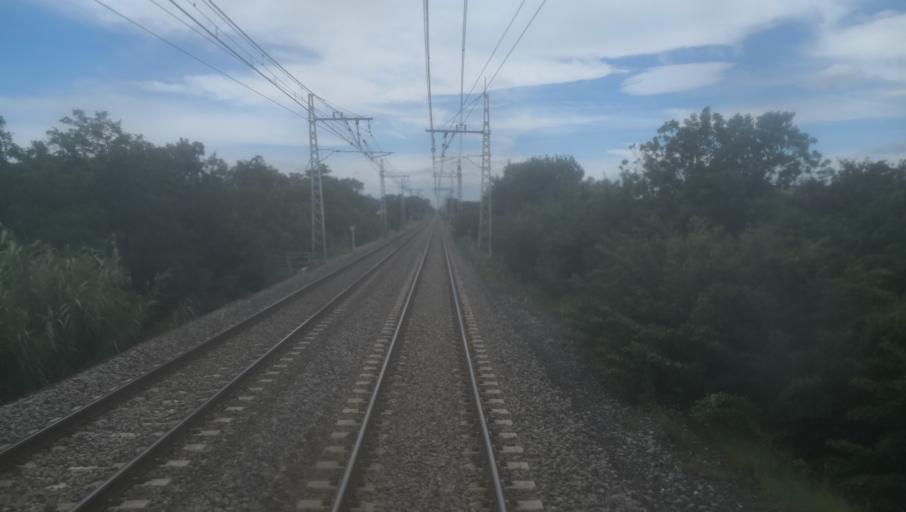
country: FR
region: Languedoc-Roussillon
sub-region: Departement de l'Herault
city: Beziers
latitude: 43.3359
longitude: 3.1997
